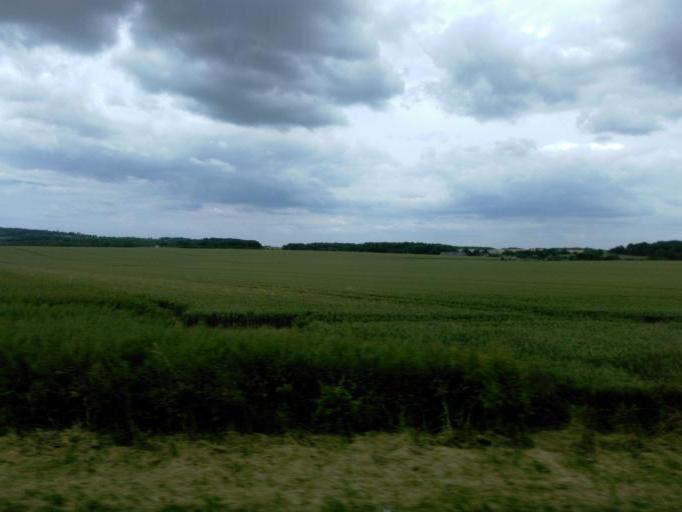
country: FR
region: Ile-de-France
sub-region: Departement du Val-d'Oise
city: Osny
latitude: 49.0987
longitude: 2.0463
